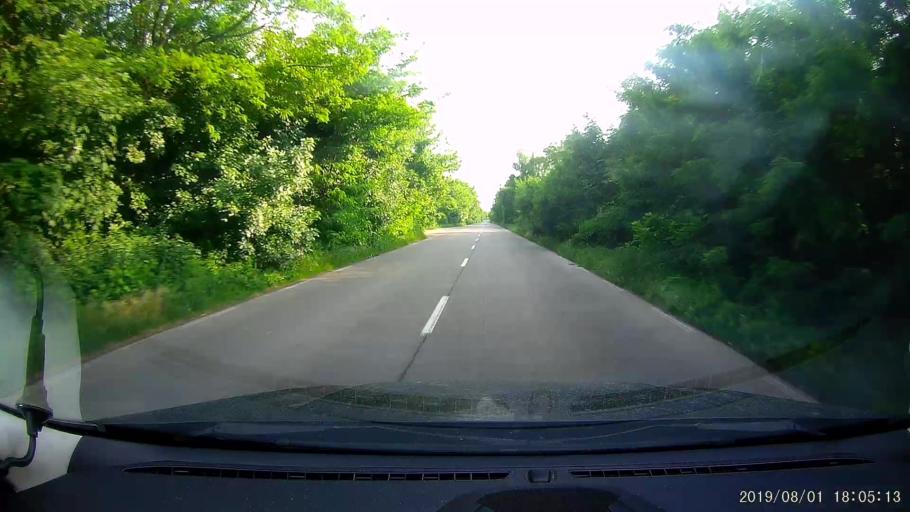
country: BG
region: Silistra
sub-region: Obshtina Alfatar
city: Alfatar
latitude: 43.8948
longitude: 27.2652
